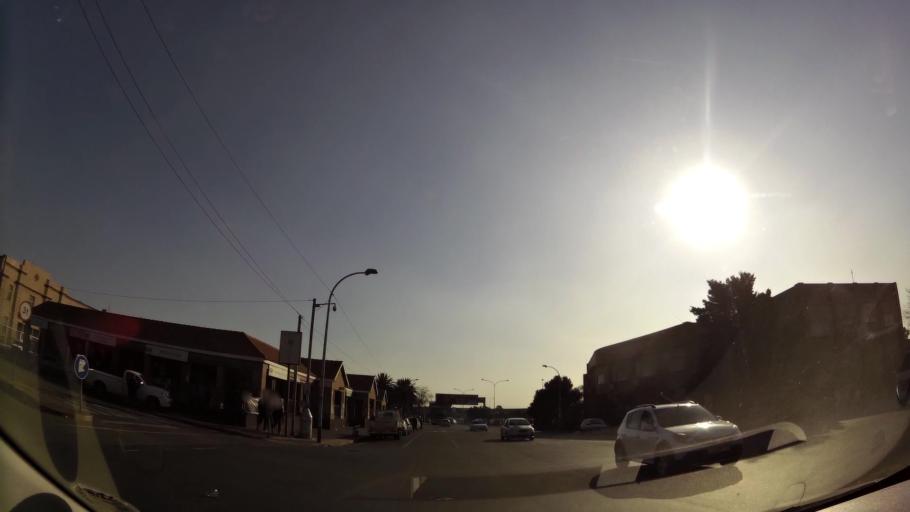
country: ZA
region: Gauteng
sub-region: West Rand District Municipality
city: Randfontein
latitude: -26.1819
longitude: 27.7000
